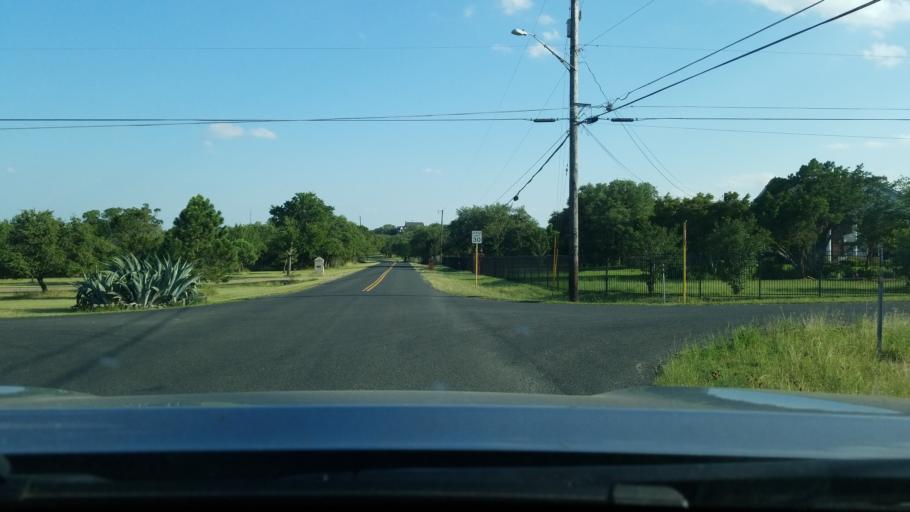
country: US
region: Texas
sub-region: Bexar County
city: Timberwood Park
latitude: 29.7053
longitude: -98.4377
